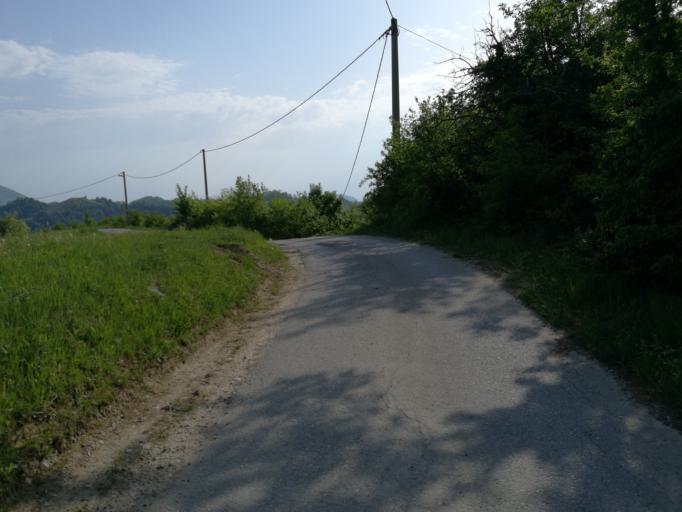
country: HR
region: Krapinsko-Zagorska
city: Radoboj
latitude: 46.2364
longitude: 15.9087
